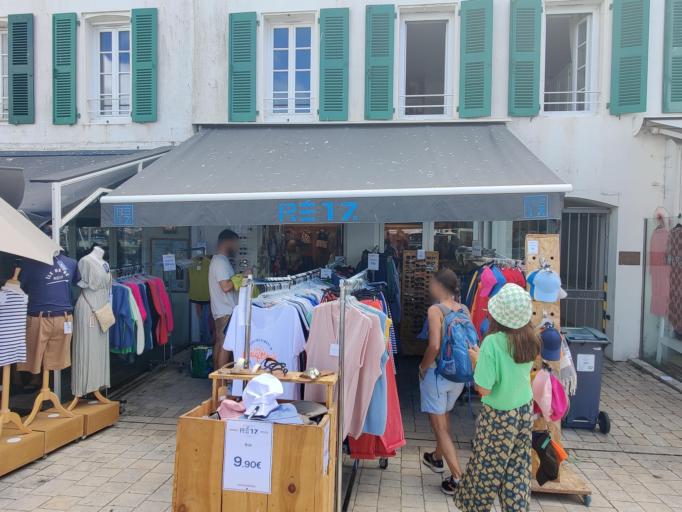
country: FR
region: Poitou-Charentes
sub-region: Departement de la Charente-Maritime
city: Saint-Martin-de-Re
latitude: 46.2048
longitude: -1.3679
